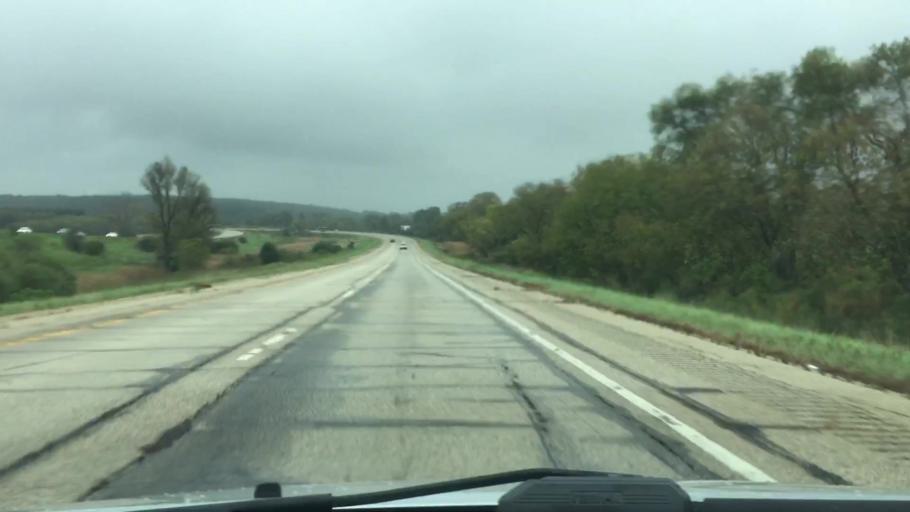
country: US
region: Wisconsin
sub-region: Walworth County
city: Como
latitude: 42.6215
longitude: -88.4631
